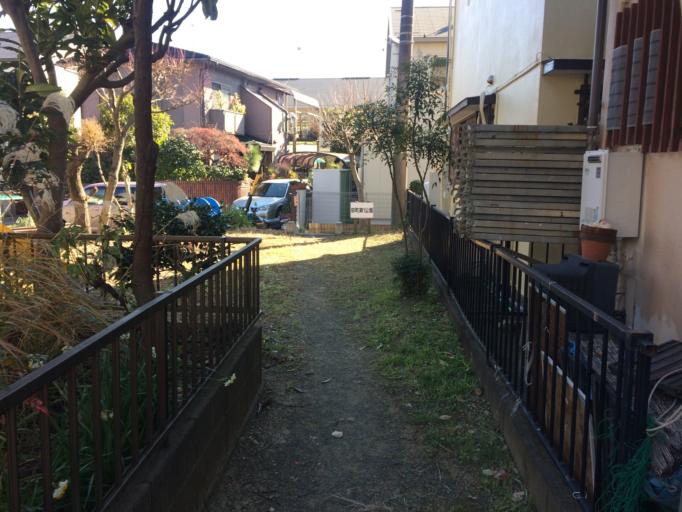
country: JP
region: Shizuoka
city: Shizuoka-shi
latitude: 35.0334
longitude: 138.4874
